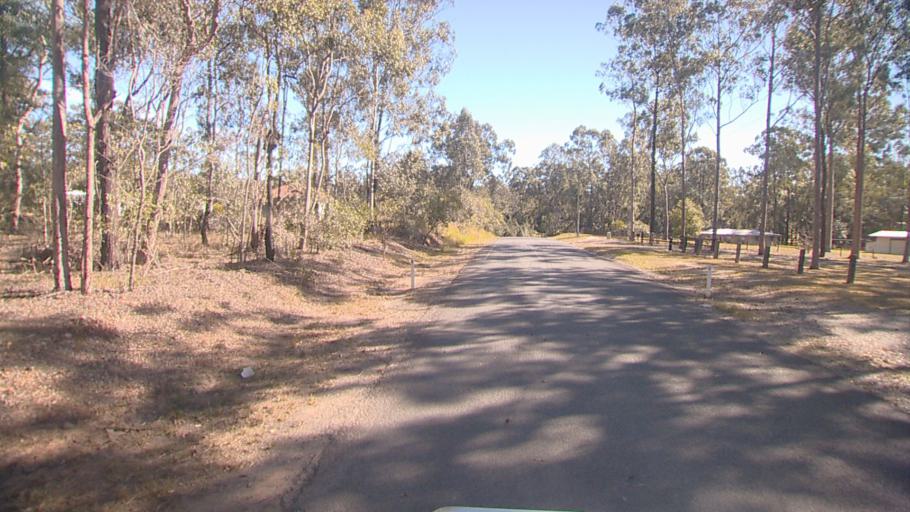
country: AU
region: Queensland
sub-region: Ipswich
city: Springfield Lakes
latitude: -27.7110
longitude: 152.9589
